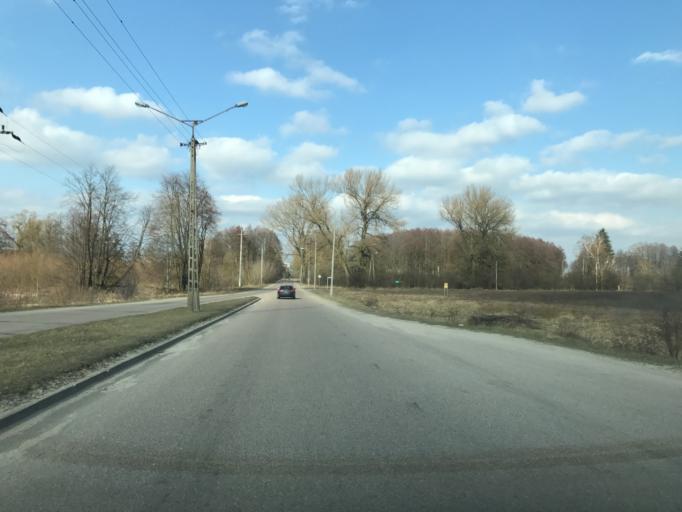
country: PL
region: Masovian Voivodeship
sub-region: Powiat mlawski
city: Mlawa
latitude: 53.0954
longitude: 20.3737
